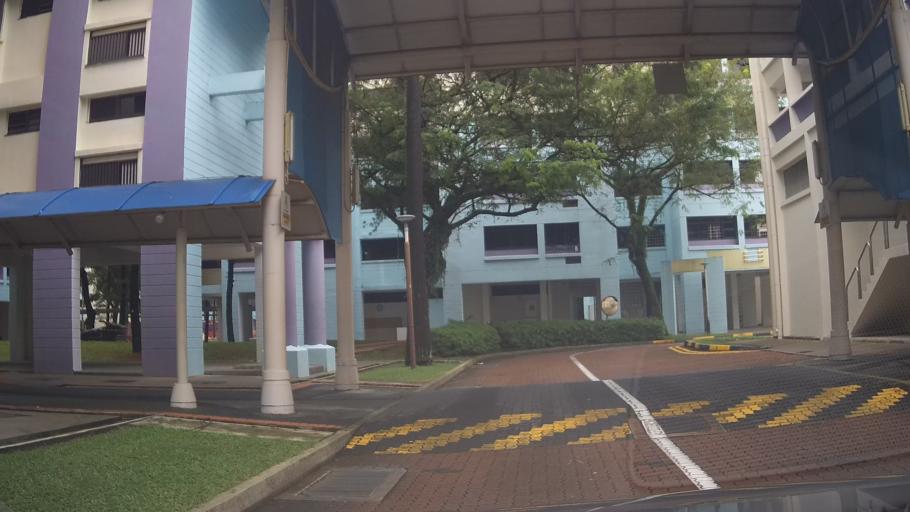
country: MY
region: Johor
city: Johor Bahru
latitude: 1.4407
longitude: 103.7982
